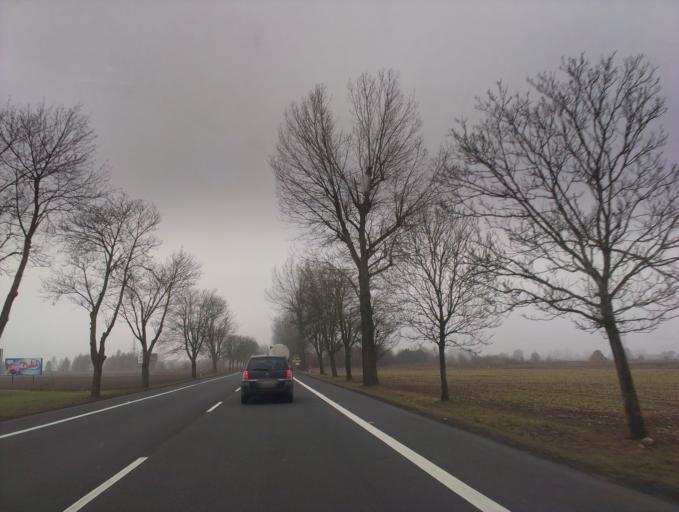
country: PL
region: Greater Poland Voivodeship
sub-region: Powiat pilski
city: Ujscie
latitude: 53.0835
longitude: 16.7321
